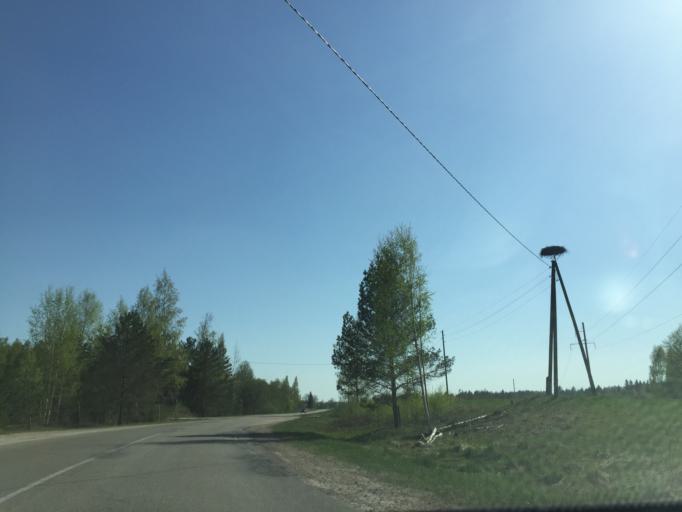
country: LV
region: Malpils
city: Malpils
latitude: 56.9258
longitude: 24.9375
